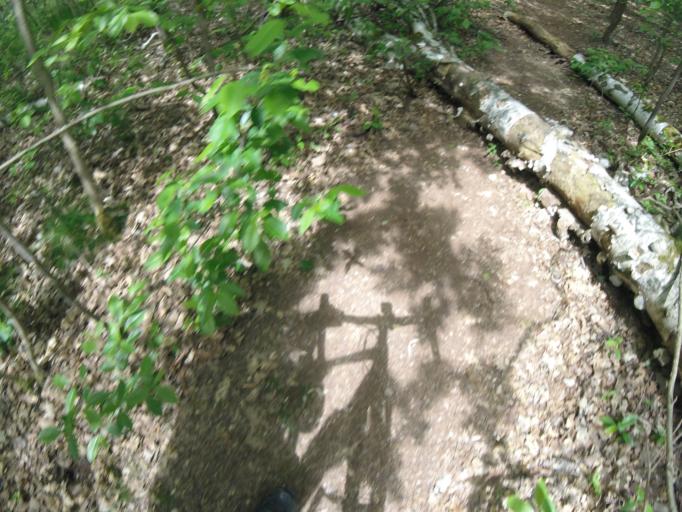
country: DE
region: Brandenburg
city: Bestensee
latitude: 52.2134
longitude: 13.6397
